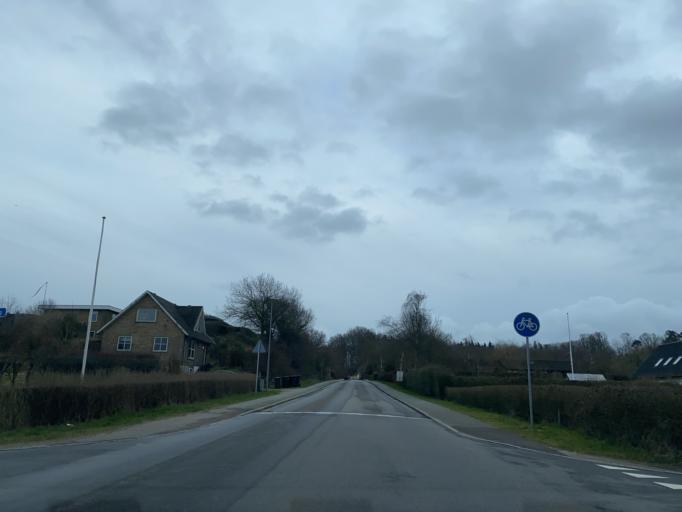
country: DK
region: Central Jutland
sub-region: Viborg Kommune
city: Bjerringbro
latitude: 56.3051
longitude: 9.5950
